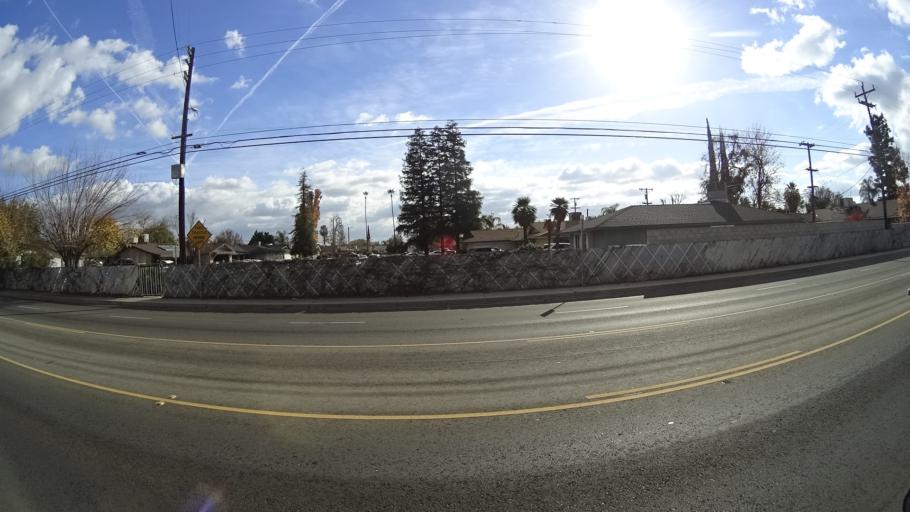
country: US
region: California
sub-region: Kern County
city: Bakersfield
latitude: 35.3322
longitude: -119.0313
